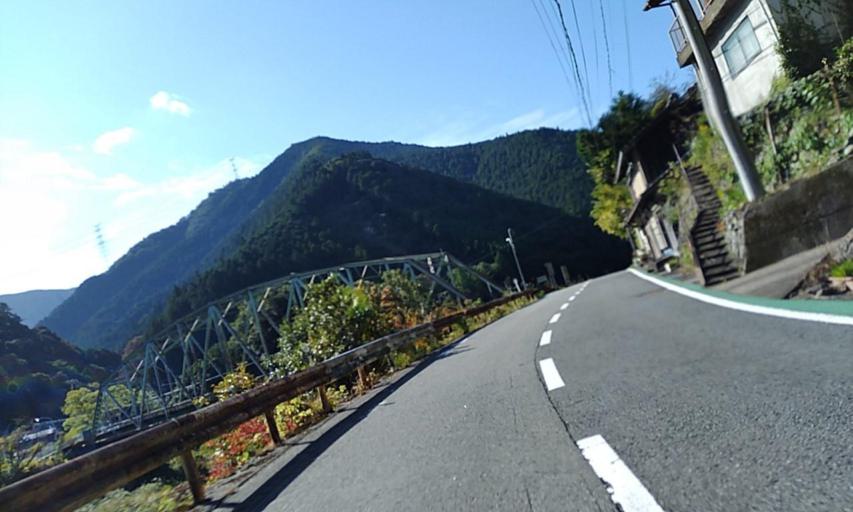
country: JP
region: Wakayama
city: Kainan
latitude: 34.0526
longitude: 135.3557
